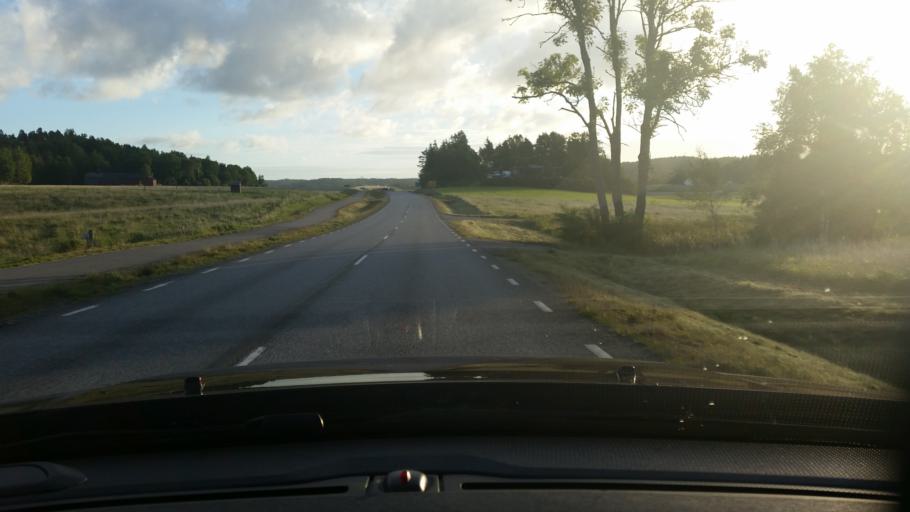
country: SE
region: Vaestra Goetaland
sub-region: Lilla Edets Kommun
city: Lodose
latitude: 58.0344
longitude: 12.1692
